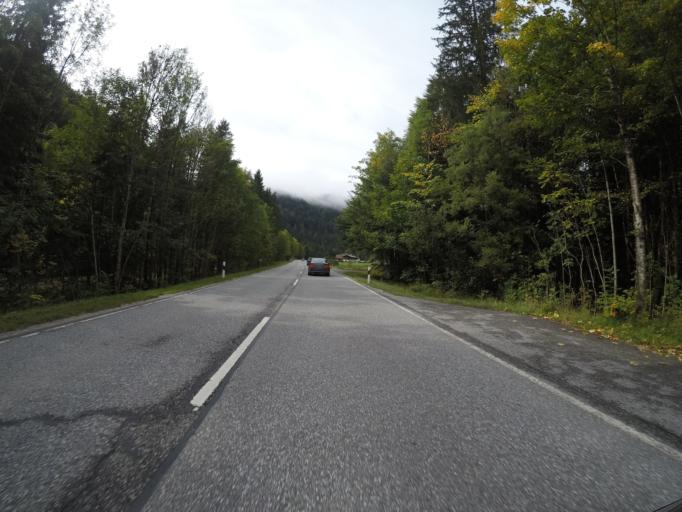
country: DE
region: Bavaria
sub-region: Upper Bavaria
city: Kreuth
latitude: 47.6140
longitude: 11.6692
